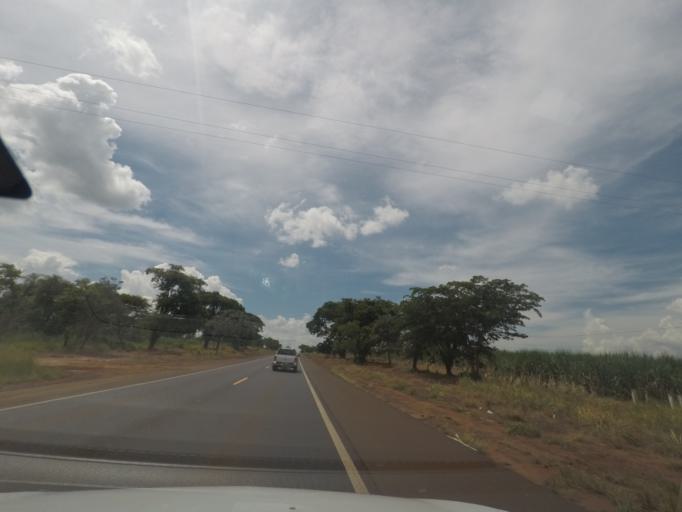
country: BR
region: Sao Paulo
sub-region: Barretos
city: Barretos
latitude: -20.2852
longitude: -48.6706
